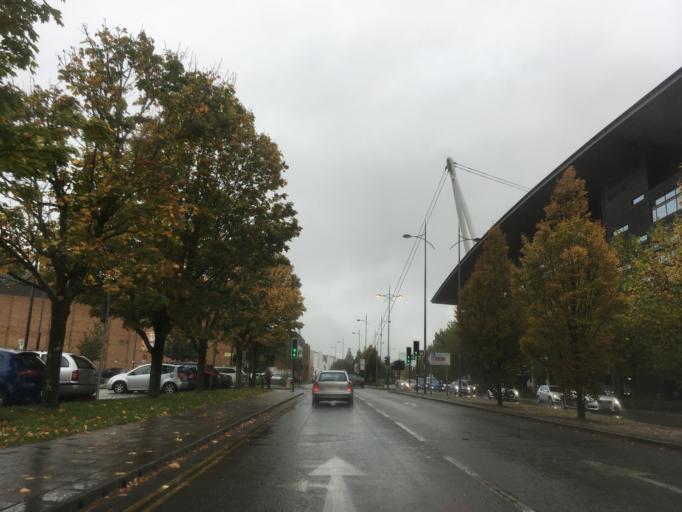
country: GB
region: Wales
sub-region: Newport
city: Newport
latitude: 51.5850
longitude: -2.9895
